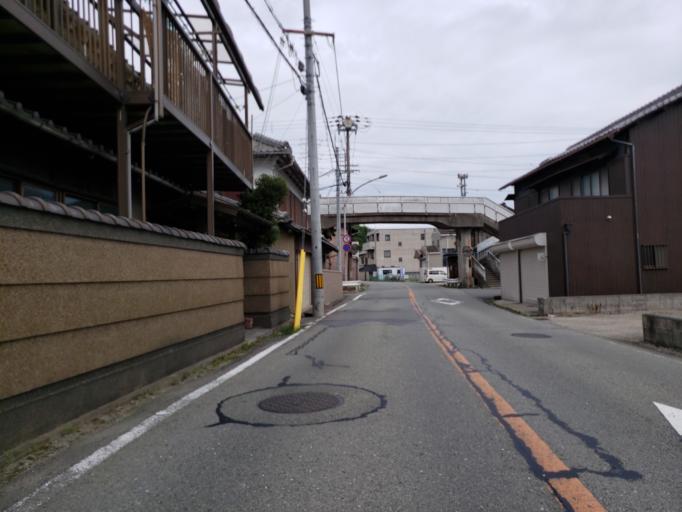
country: JP
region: Hyogo
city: Shirahamacho-usazakiminami
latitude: 34.7883
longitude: 134.6922
